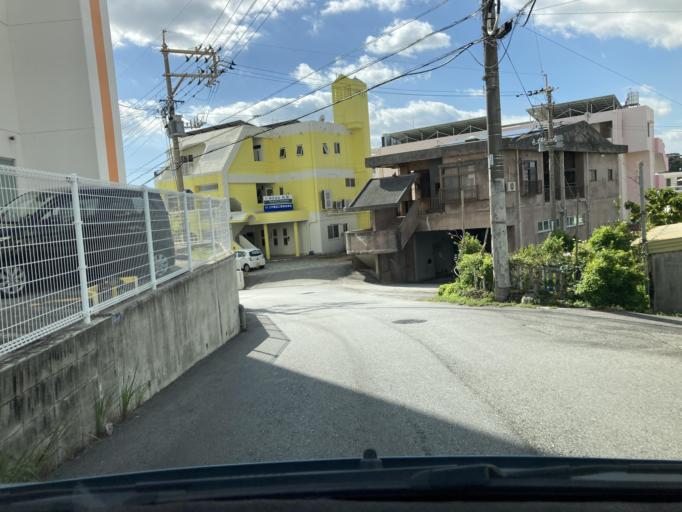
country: JP
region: Okinawa
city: Okinawa
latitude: 26.3279
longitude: 127.8170
